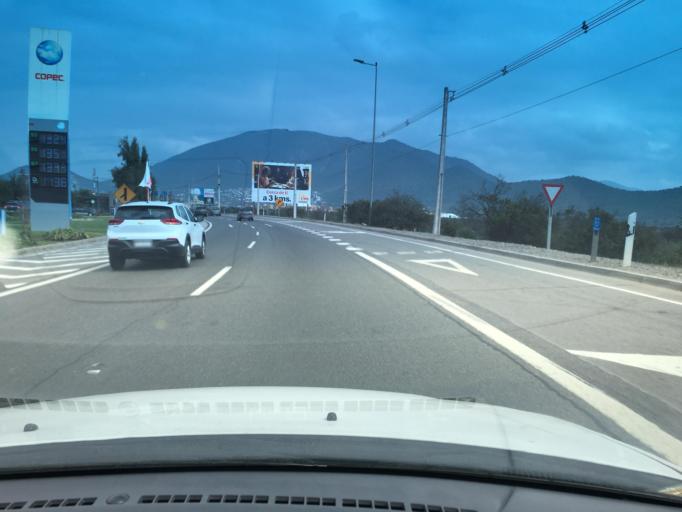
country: CL
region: Santiago Metropolitan
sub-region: Provincia de Santiago
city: Lo Prado
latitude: -33.4336
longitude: -70.8107
